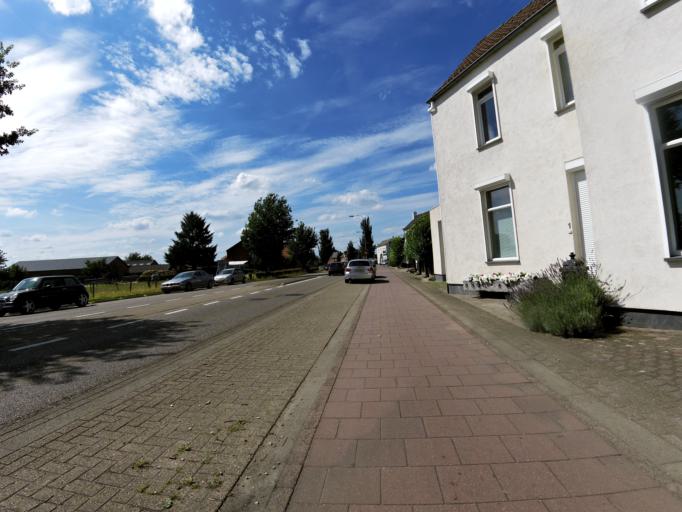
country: NL
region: Limburg
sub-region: Gemeente Schinnen
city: Doenrade
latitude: 50.9714
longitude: 5.8912
